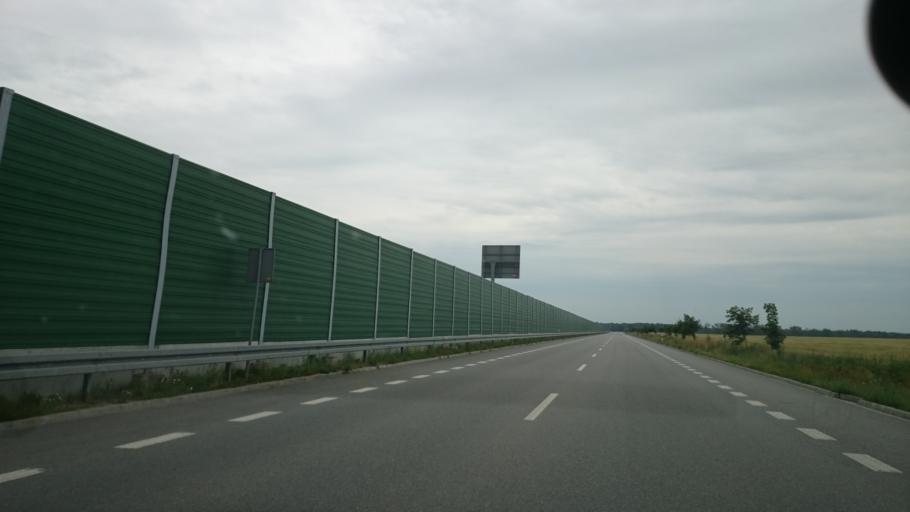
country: PL
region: Opole Voivodeship
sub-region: Powiat brzeski
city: Grodkow
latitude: 50.6832
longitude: 17.3892
